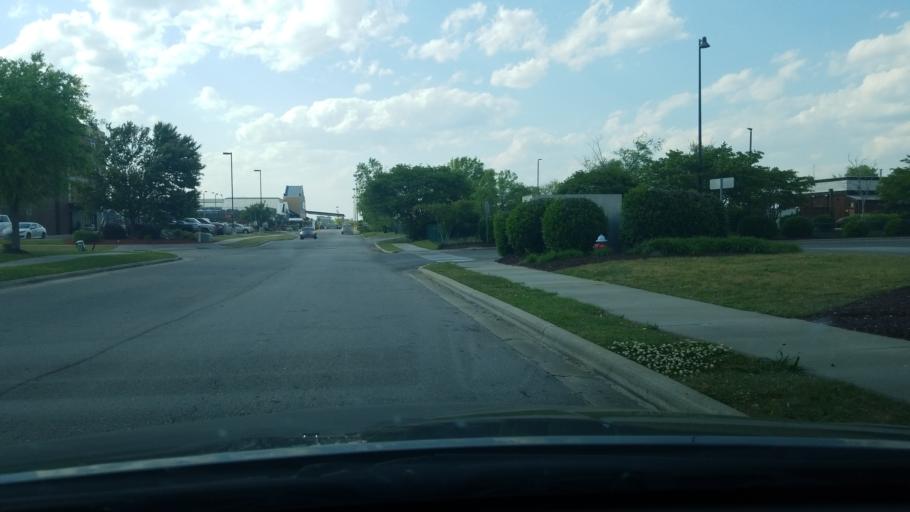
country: US
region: North Carolina
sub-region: Onslow County
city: Pumpkin Center
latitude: 34.7818
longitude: -77.3993
